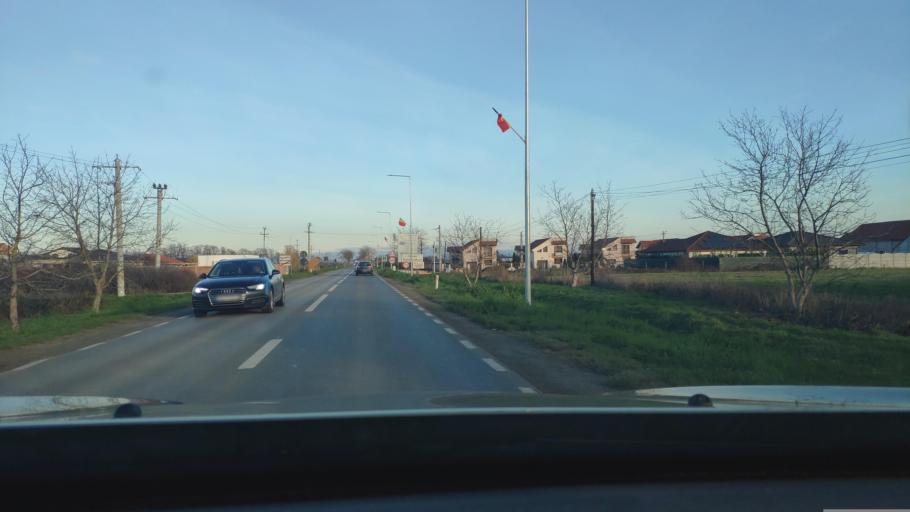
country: RO
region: Satu Mare
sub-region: Comuna Paulesti
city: Paulesti
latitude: 47.7970
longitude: 22.9383
